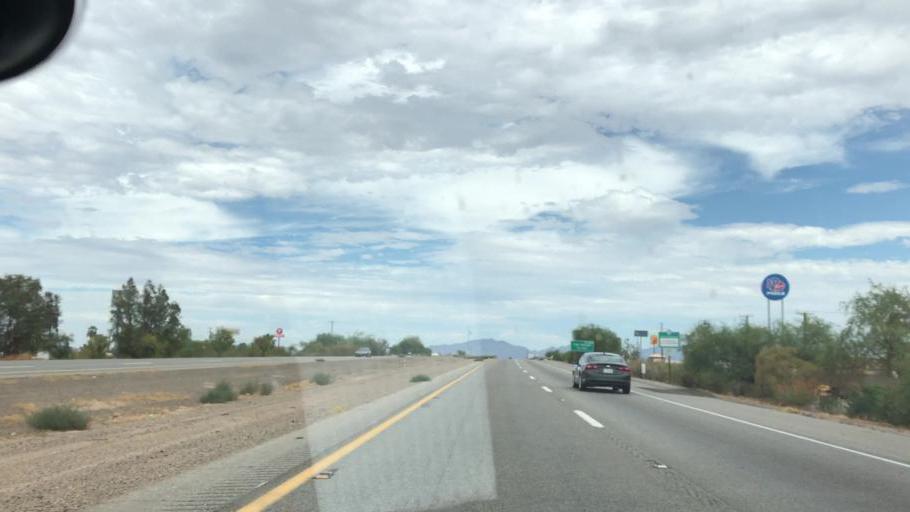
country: US
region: California
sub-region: Riverside County
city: Blythe
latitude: 33.6069
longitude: -114.6081
